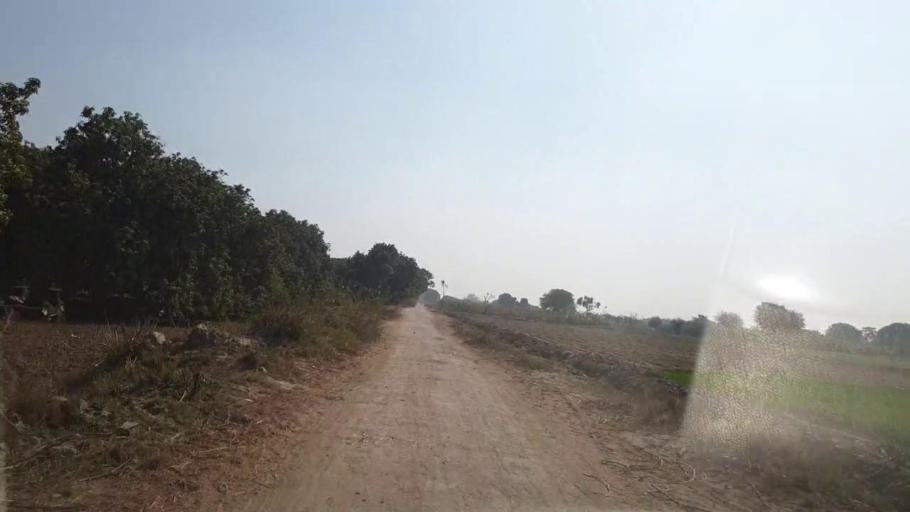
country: PK
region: Sindh
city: Matiari
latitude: 25.5105
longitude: 68.4623
